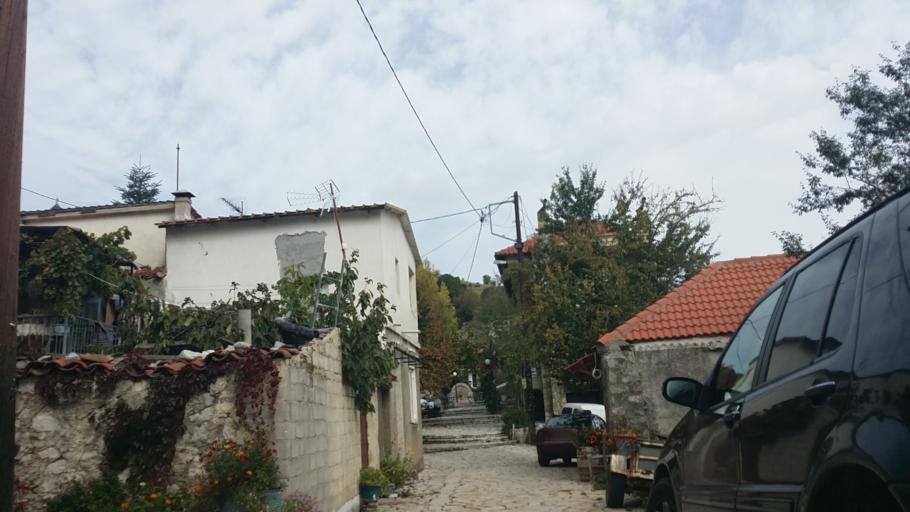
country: GR
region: Central Greece
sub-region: Nomos Voiotias
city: Kyriaki
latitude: 38.3649
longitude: 22.8397
